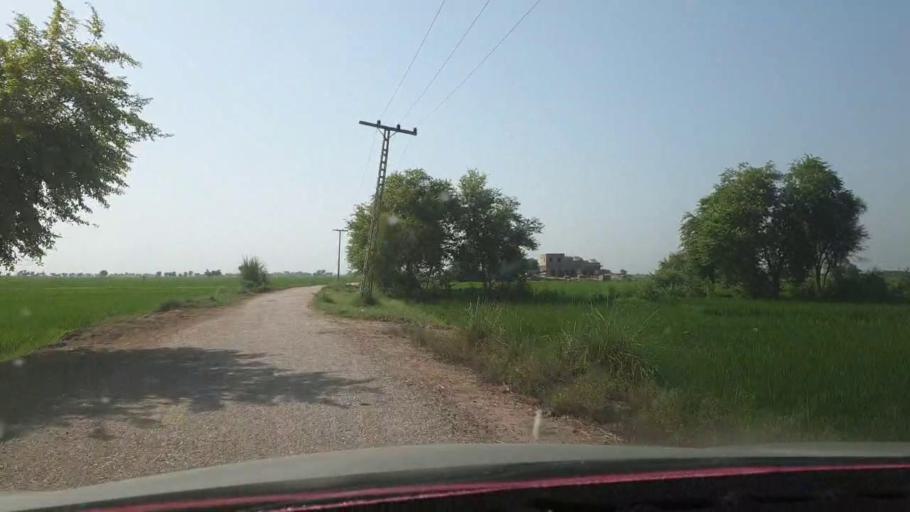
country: PK
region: Sindh
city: Nasirabad
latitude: 27.3788
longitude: 67.8840
